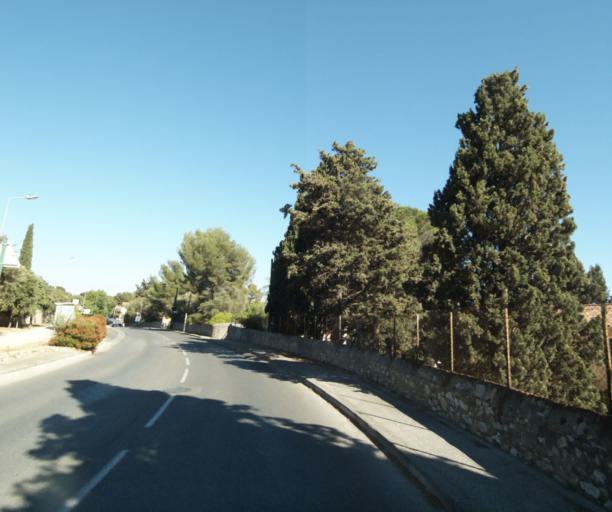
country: FR
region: Provence-Alpes-Cote d'Azur
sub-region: Departement du Var
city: La Garde
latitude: 43.1081
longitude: 5.9830
